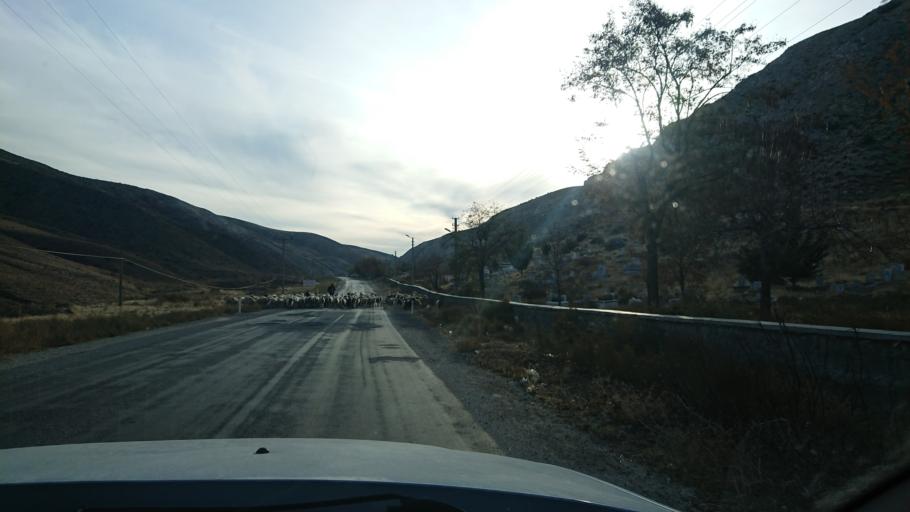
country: TR
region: Ankara
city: Sereflikochisar
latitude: 38.7604
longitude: 33.6970
